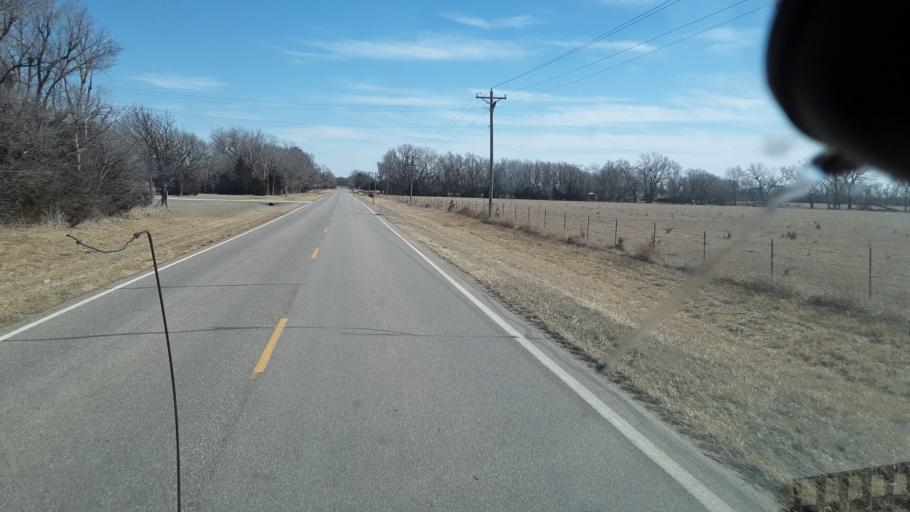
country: US
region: Kansas
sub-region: Reno County
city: Buhler
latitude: 38.1593
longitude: -97.8656
